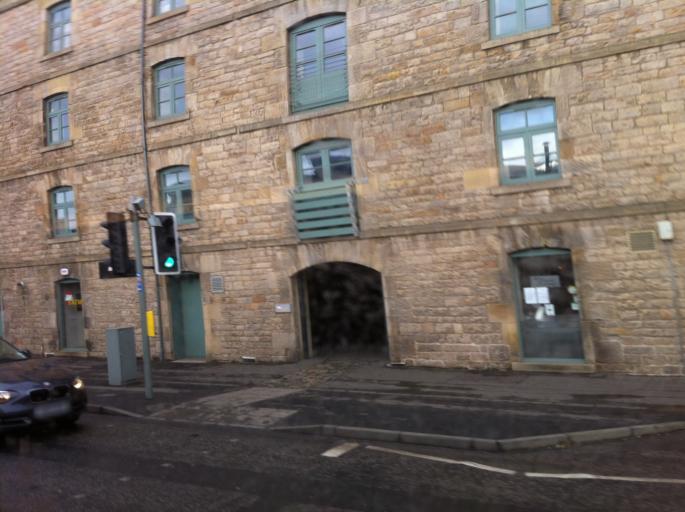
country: GB
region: Scotland
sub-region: West Lothian
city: Seafield
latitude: 55.9770
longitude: -3.1734
